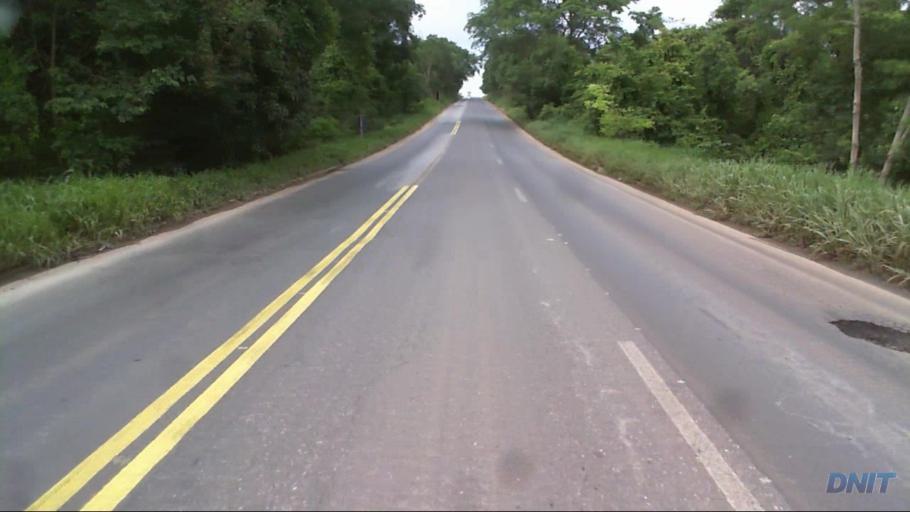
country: BR
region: Goias
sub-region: Uruacu
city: Uruacu
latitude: -14.6025
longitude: -49.1657
